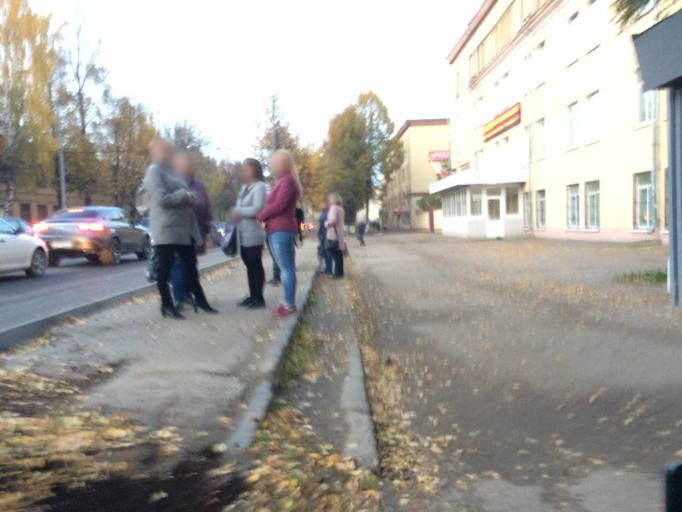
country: RU
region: Mariy-El
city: Yoshkar-Ola
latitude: 56.6143
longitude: 47.8825
